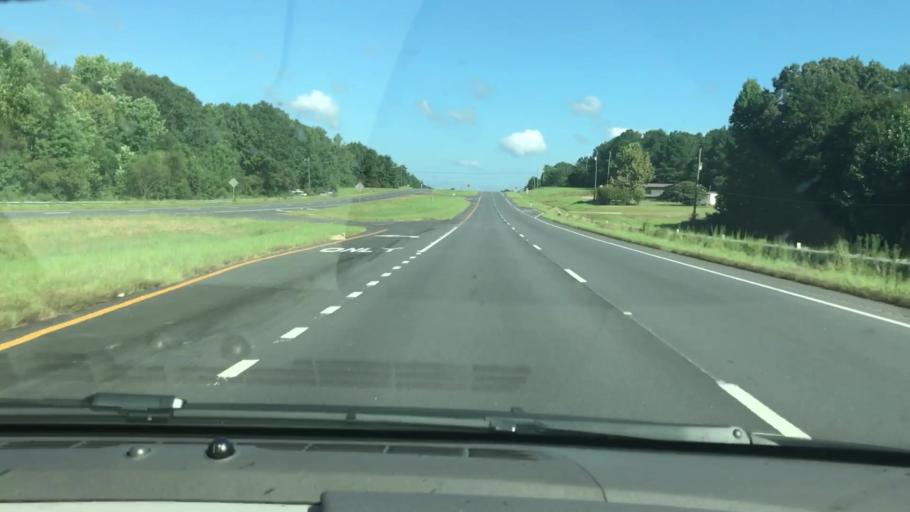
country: US
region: Alabama
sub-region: Barbour County
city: Eufaula
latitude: 32.0346
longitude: -85.1241
